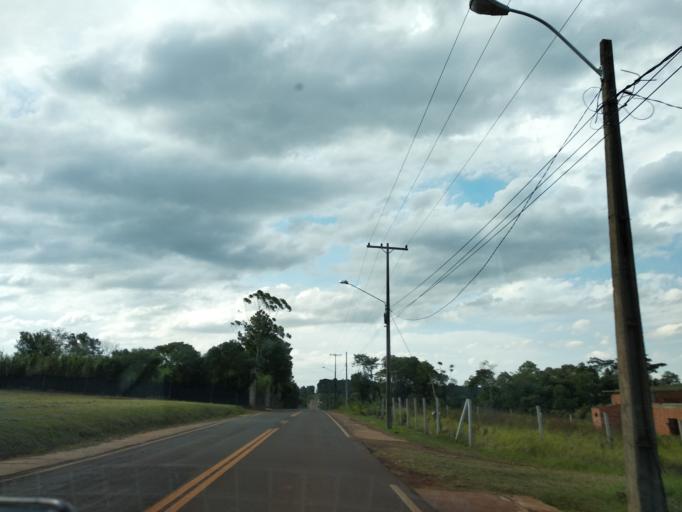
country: PY
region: Itapua
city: San Juan del Parana
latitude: -27.2903
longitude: -55.9557
